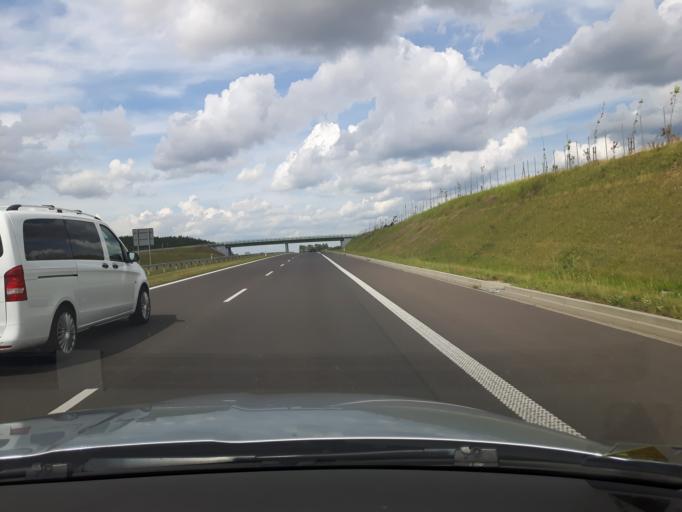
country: PL
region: Warmian-Masurian Voivodeship
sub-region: Powiat nidzicki
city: Nidzica
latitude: 53.3188
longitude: 20.4390
